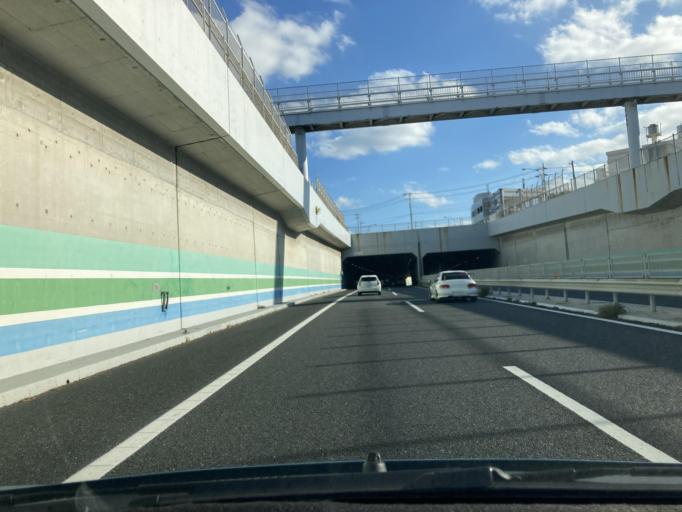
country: JP
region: Okinawa
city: Okinawa
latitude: 26.3240
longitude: 127.7882
